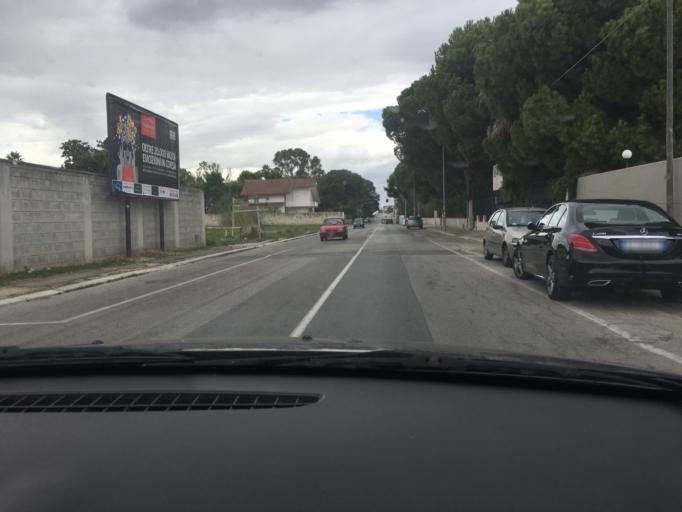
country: IT
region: Apulia
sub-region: Provincia di Bari
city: Bari
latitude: 41.1317
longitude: 16.8340
